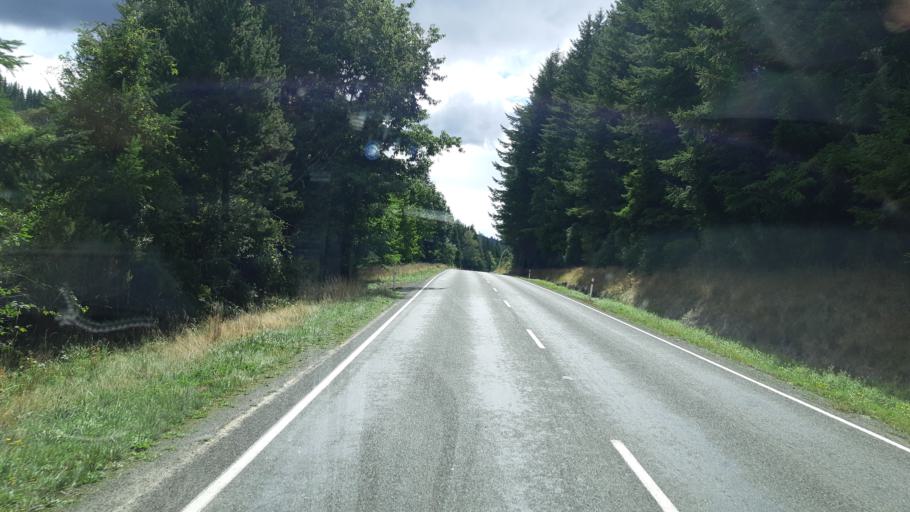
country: NZ
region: Tasman
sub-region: Tasman District
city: Wakefield
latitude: -41.5804
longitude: 172.7684
